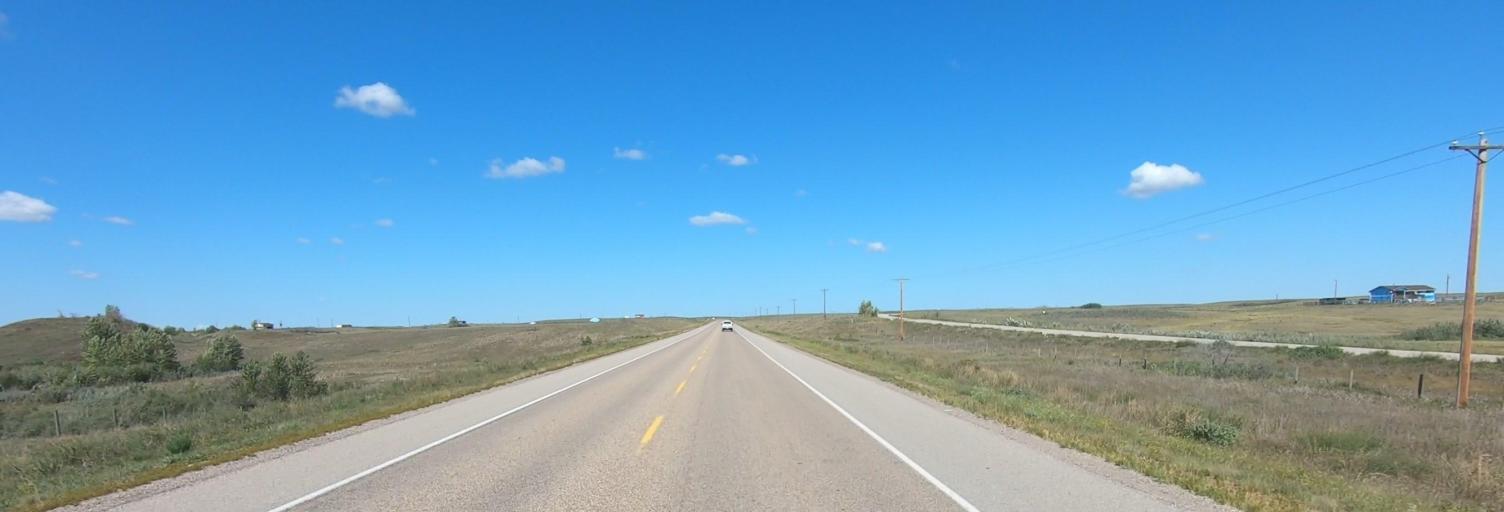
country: CA
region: Alberta
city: Strathmore
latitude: 50.8601
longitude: -113.1392
